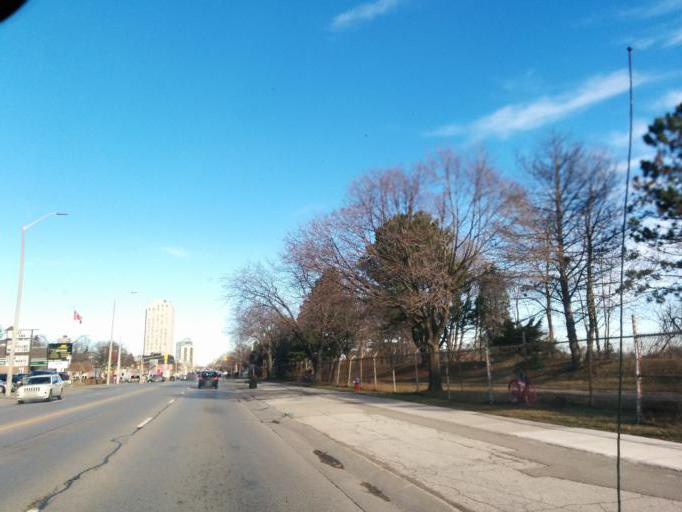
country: CA
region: Ontario
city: Mississauga
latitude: 43.5450
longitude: -79.5930
